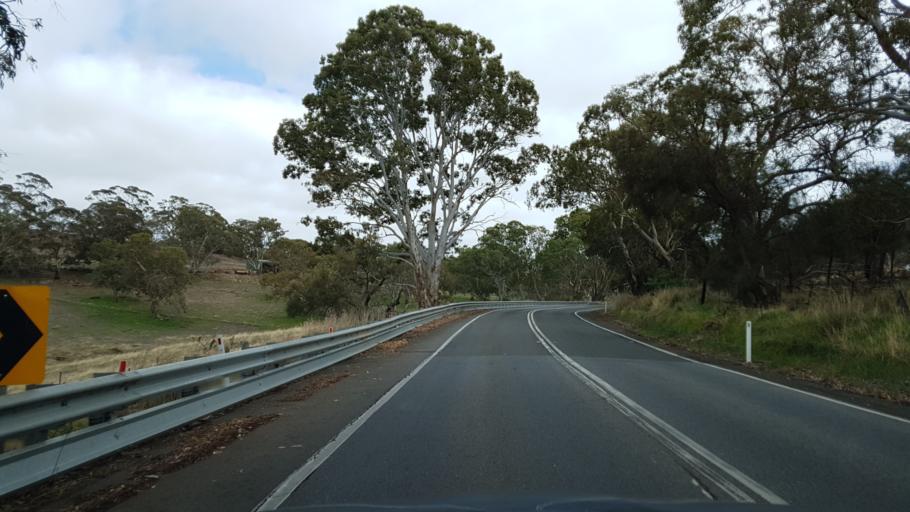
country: AU
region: South Australia
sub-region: Mount Barker
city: Nairne
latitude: -35.0437
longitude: 138.9440
